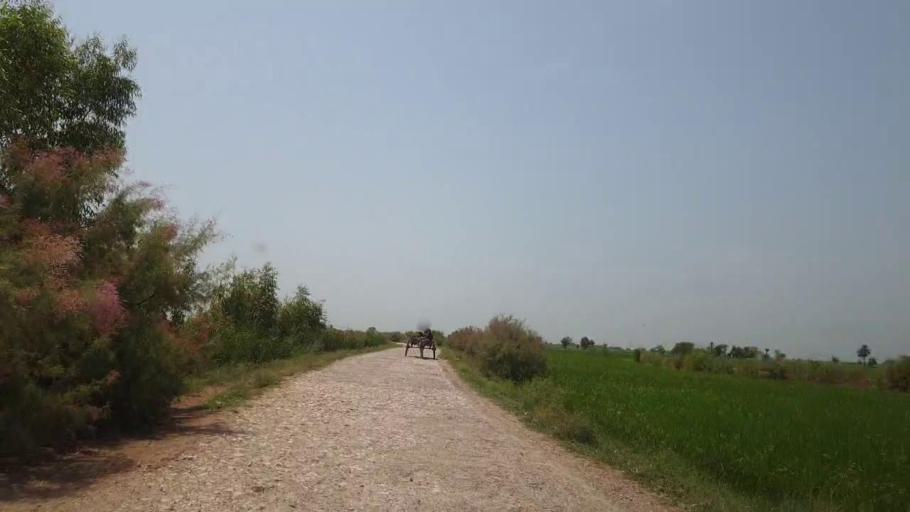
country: PK
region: Sindh
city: Shikarpur
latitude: 27.9024
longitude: 68.6328
